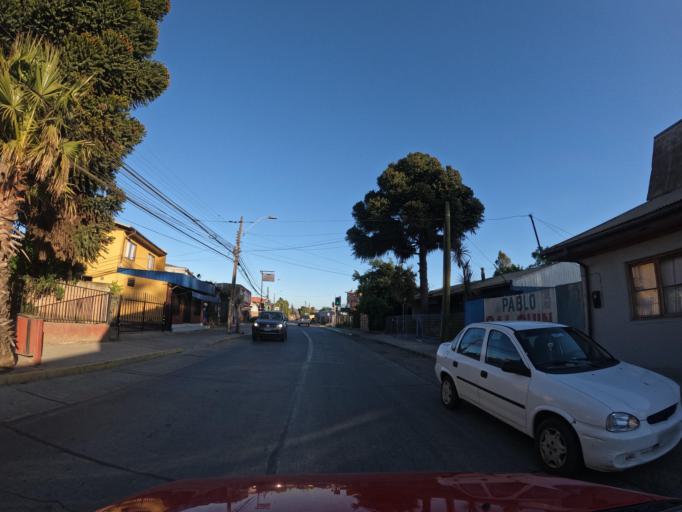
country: CL
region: Maule
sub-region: Provincia de Talca
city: Constitucion
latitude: -34.9861
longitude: -71.9868
